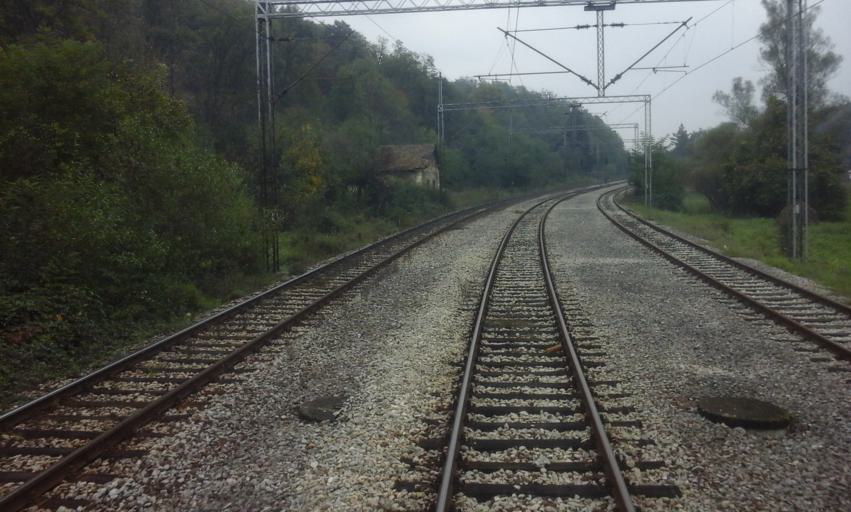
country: RS
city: Rusanj
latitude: 44.6448
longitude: 20.5332
